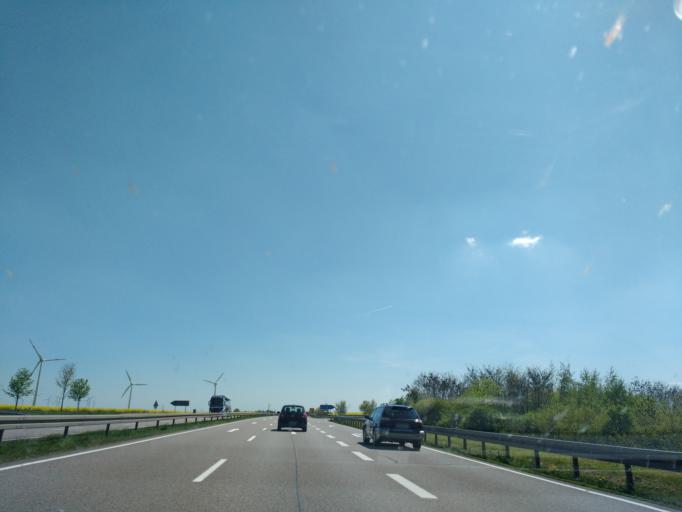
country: DE
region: Saxony-Anhalt
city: Nessa
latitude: 51.1759
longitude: 12.0044
